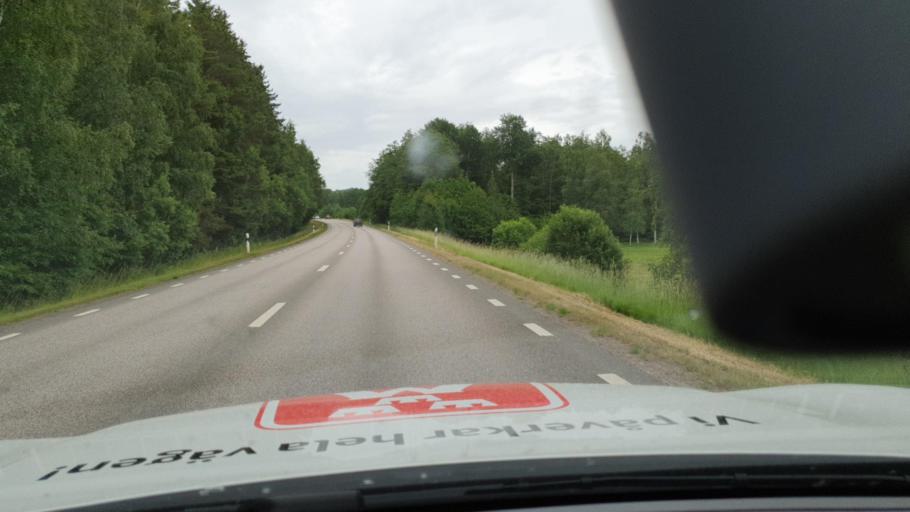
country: SE
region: Vaestra Goetaland
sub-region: Tibro Kommun
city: Tibro
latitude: 58.3425
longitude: 14.1614
